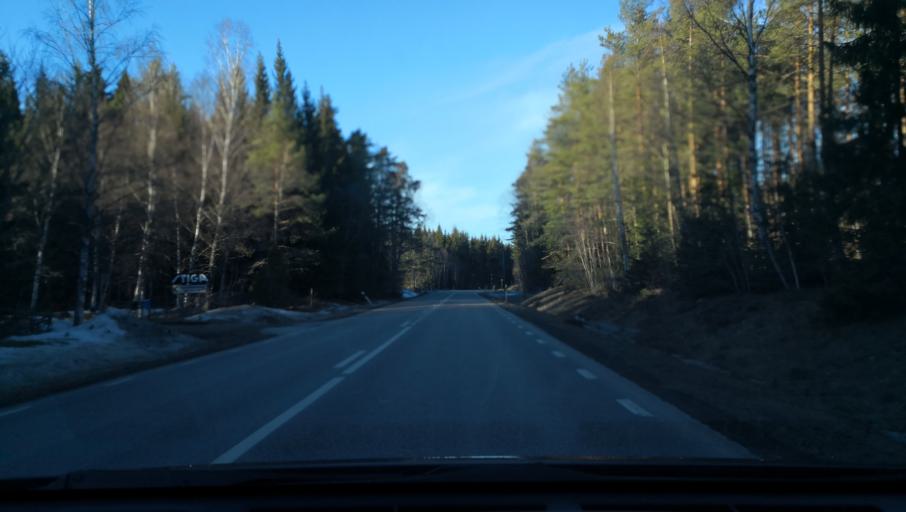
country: SE
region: Uppsala
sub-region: Osthammars Kommun
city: Gimo
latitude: 60.2092
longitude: 18.1923
